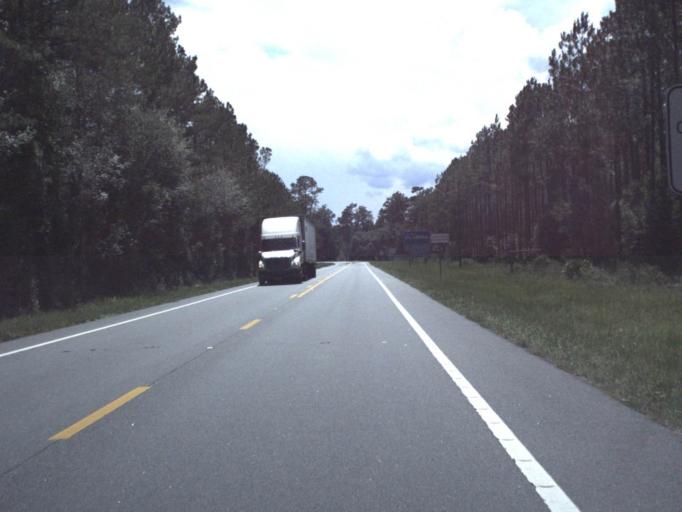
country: US
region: Florida
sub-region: Hamilton County
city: Jasper
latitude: 30.5964
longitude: -82.6720
